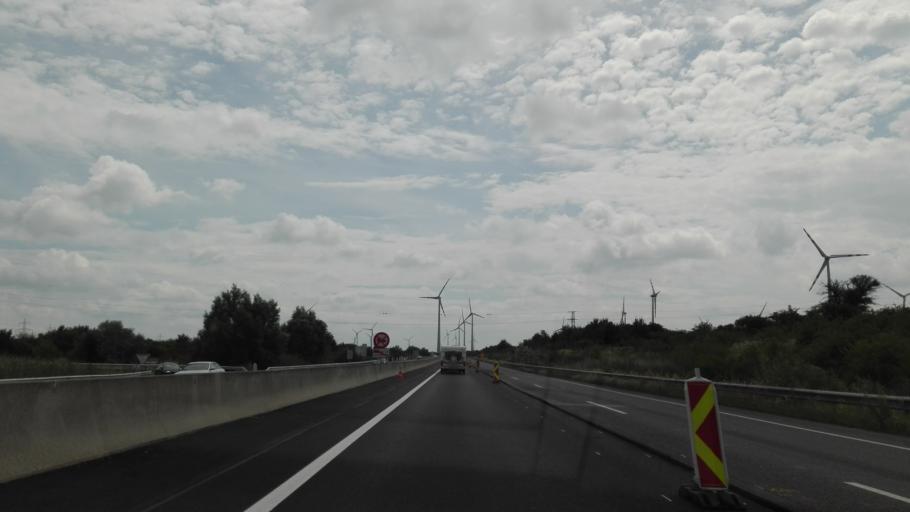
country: AT
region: Burgenland
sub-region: Politischer Bezirk Neusiedl am See
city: Zurndorf
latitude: 47.9313
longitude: 16.9967
